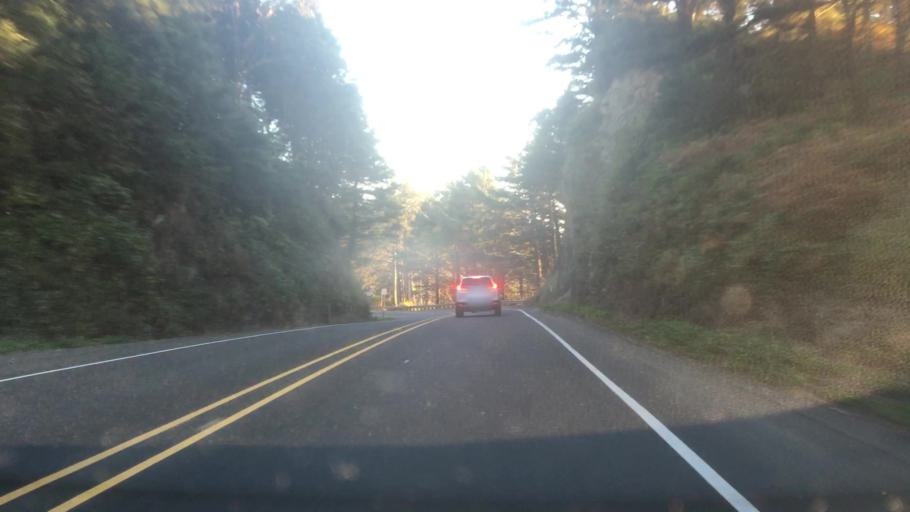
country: US
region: Oregon
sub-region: Clatsop County
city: Cannon Beach
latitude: 45.8487
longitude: -123.9606
